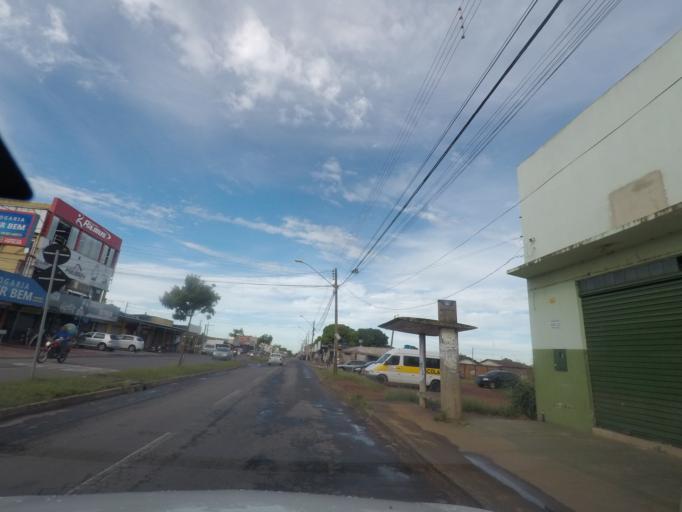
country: BR
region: Goias
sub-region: Aparecida De Goiania
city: Aparecida de Goiania
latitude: -16.7810
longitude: -49.3566
